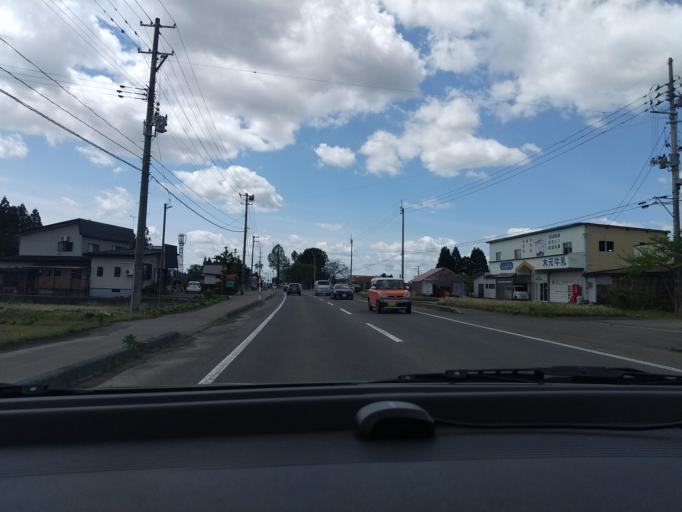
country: JP
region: Akita
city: Kakunodatemachi
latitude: 39.5728
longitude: 140.5627
